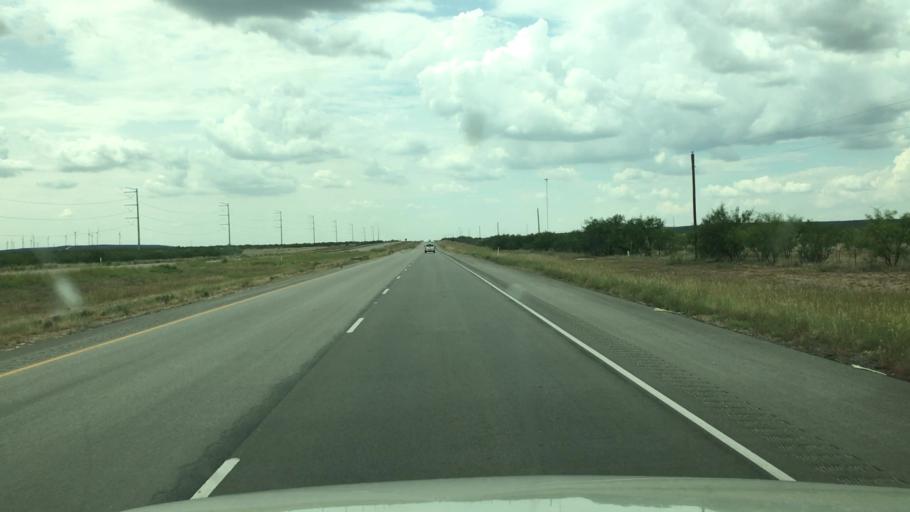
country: US
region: Texas
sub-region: Glasscock County
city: Garden City
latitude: 31.9721
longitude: -101.2435
